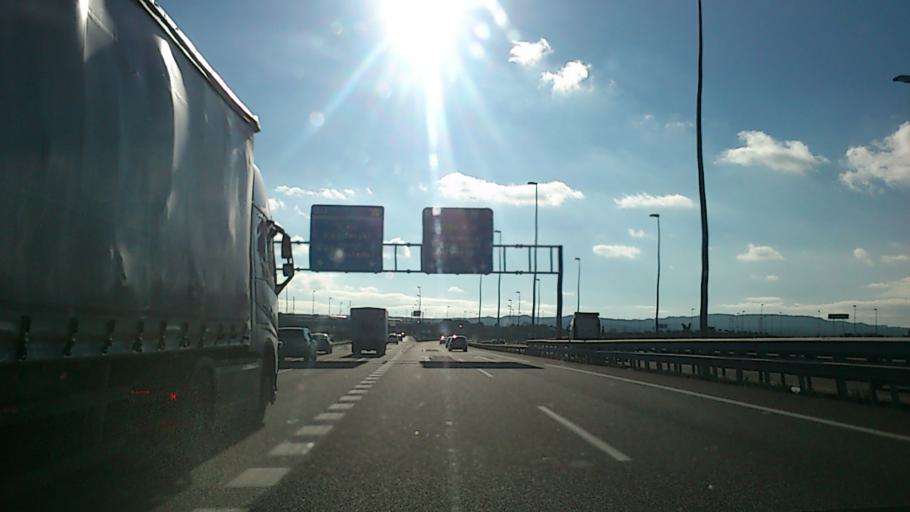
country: ES
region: Aragon
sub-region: Provincia de Zaragoza
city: Montecanal
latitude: 41.6403
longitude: -0.9722
